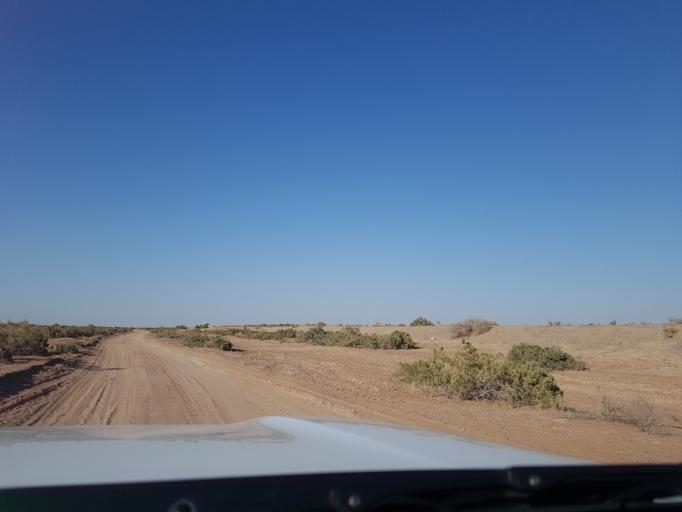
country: IR
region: Razavi Khorasan
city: Sarakhs
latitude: 36.9881
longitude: 61.3874
